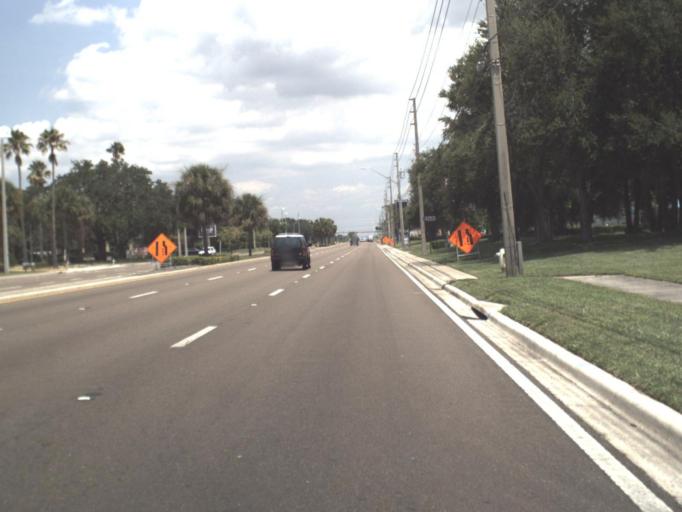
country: US
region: Florida
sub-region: Pinellas County
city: Gulfport
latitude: 27.7281
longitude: -82.6792
